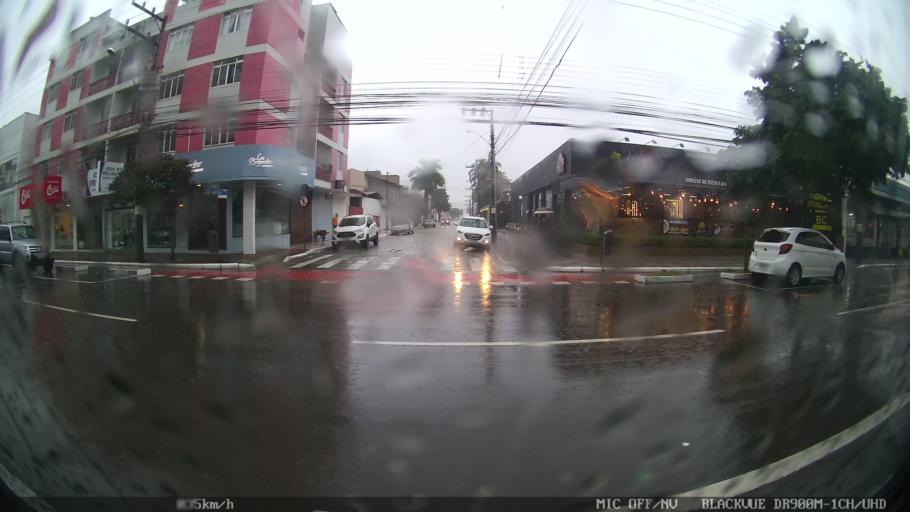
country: BR
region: Santa Catarina
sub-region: Balneario Camboriu
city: Balneario Camboriu
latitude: -26.9969
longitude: -48.6337
